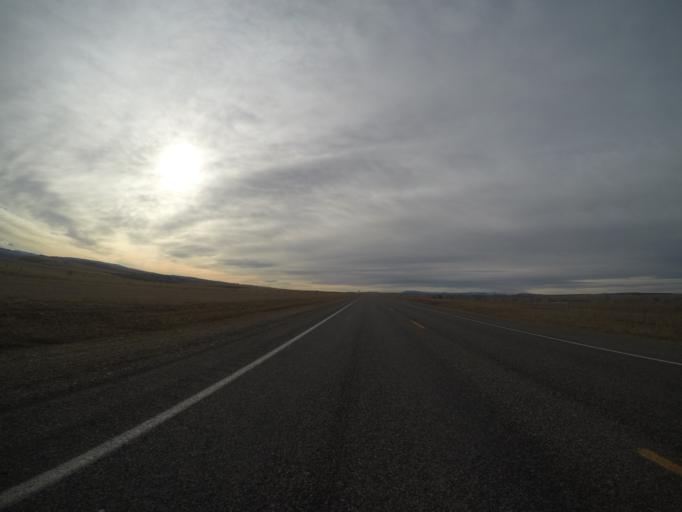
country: US
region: Montana
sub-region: Yellowstone County
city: Laurel
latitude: 45.5798
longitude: -108.8428
